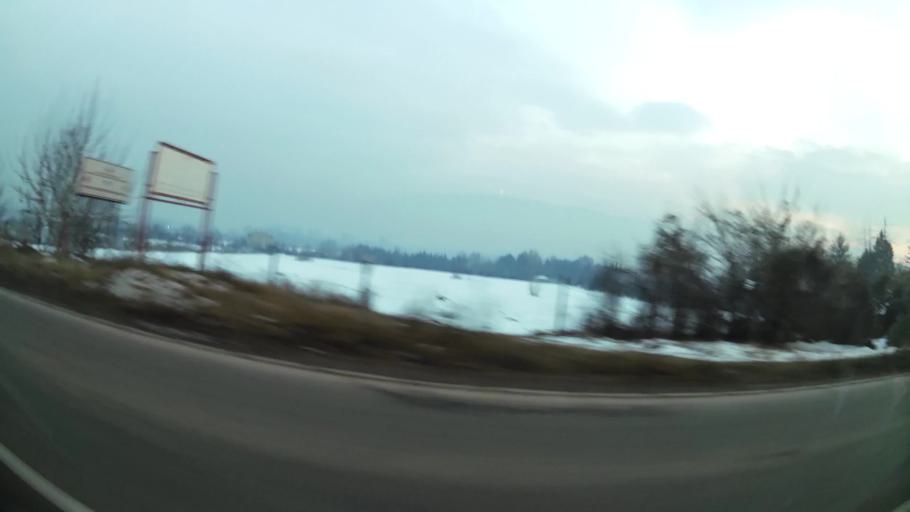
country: MK
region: Suto Orizari
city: Suto Orizare
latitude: 42.0149
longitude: 21.3973
